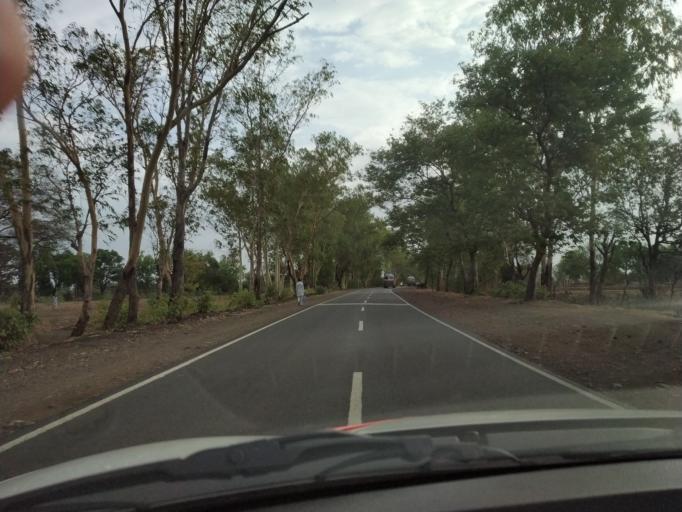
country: IN
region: Madhya Pradesh
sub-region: Shajapur
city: Agar
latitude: 23.5863
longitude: 75.9349
